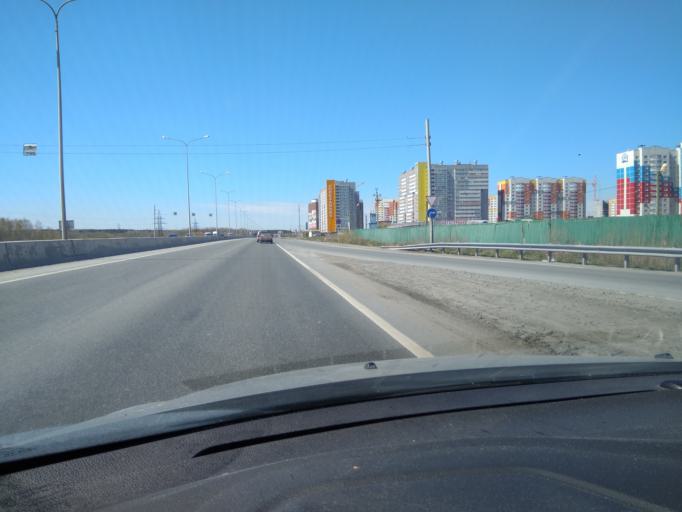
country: RU
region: Tjumen
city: Tyumen
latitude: 57.1309
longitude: 65.4778
